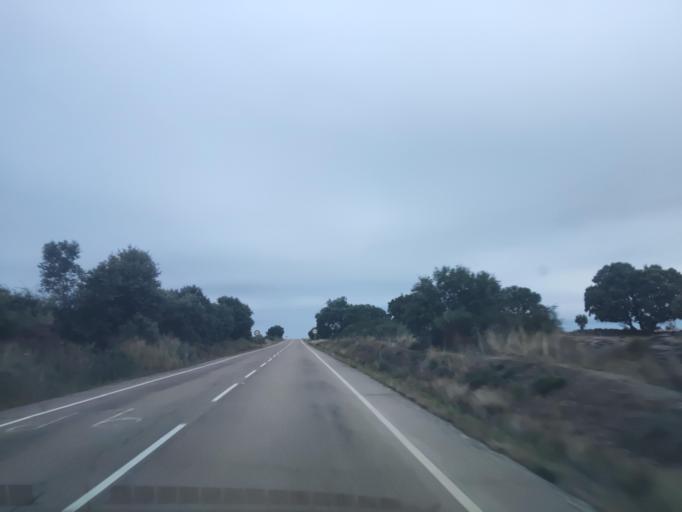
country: ES
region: Castille and Leon
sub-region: Provincia de Salamanca
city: Hinojosa de Duero
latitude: 40.9650
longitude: -6.8070
